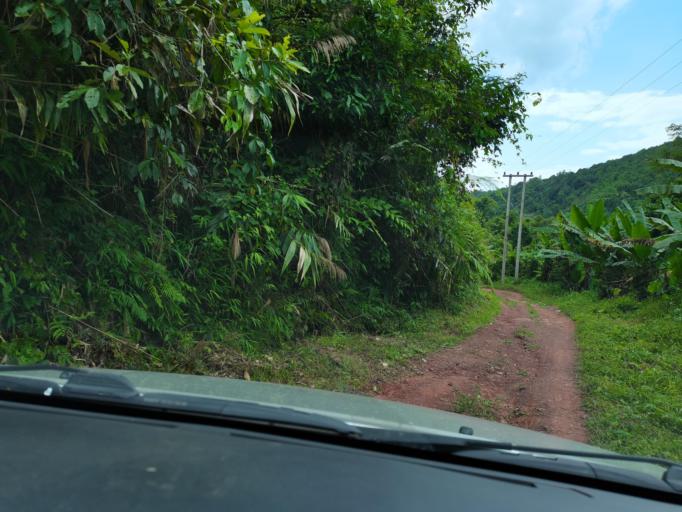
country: LA
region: Loungnamtha
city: Muang Nale
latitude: 20.5126
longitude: 101.0792
